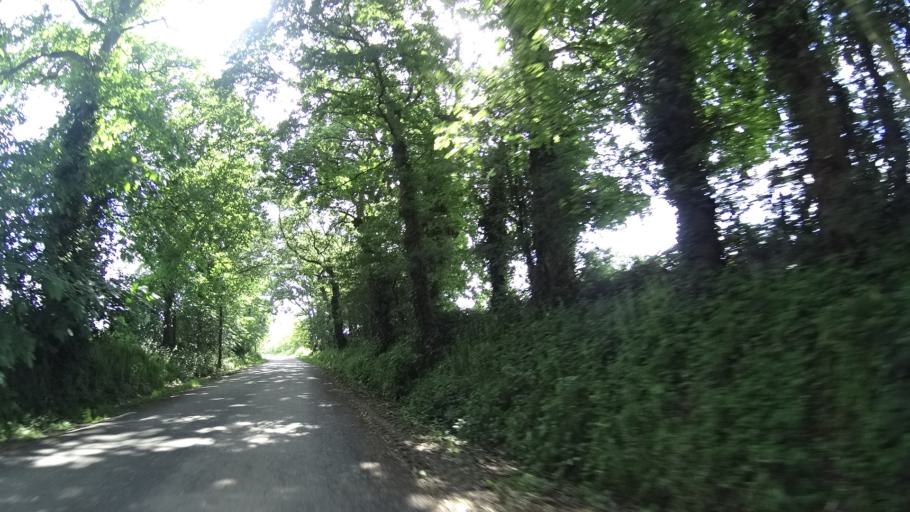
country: FR
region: Brittany
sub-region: Departement d'Ille-et-Vilaine
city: Melesse
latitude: 48.2074
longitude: -1.7140
